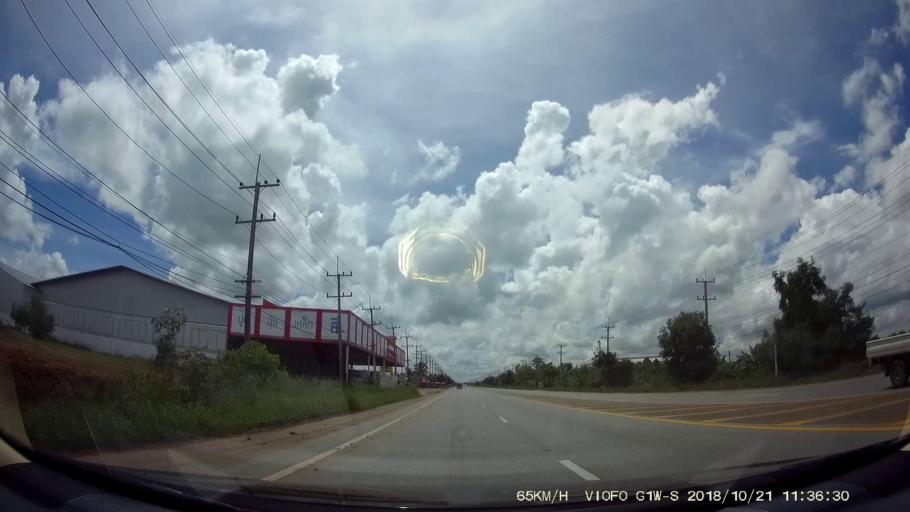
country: TH
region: Chaiyaphum
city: Chaiyaphum
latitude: 15.7188
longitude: 102.0162
